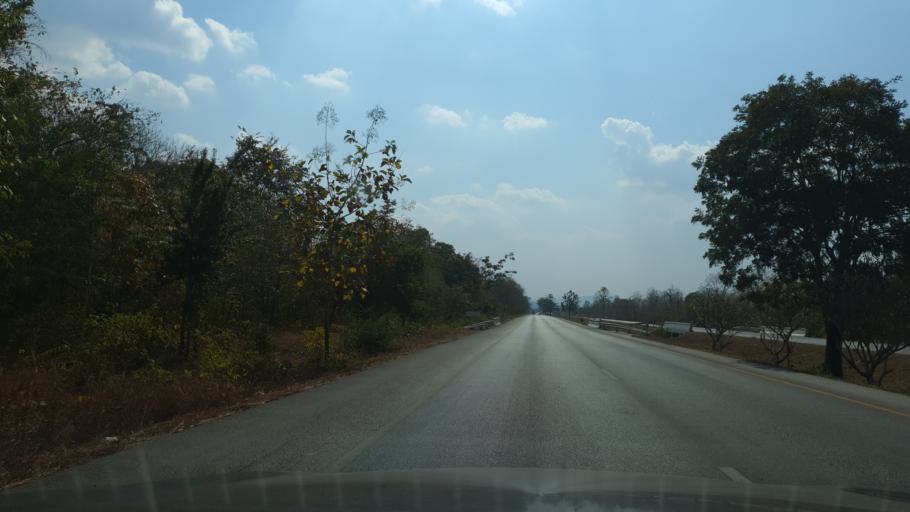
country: TH
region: Lampang
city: Mae Phrik
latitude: 17.4381
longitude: 99.1588
